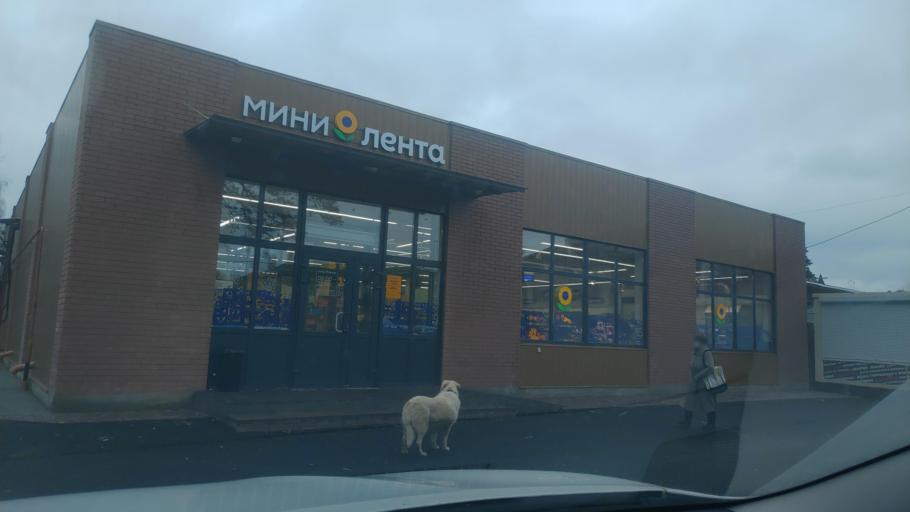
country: RU
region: Moskovskaya
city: Snegiri
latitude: 55.8881
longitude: 37.0320
